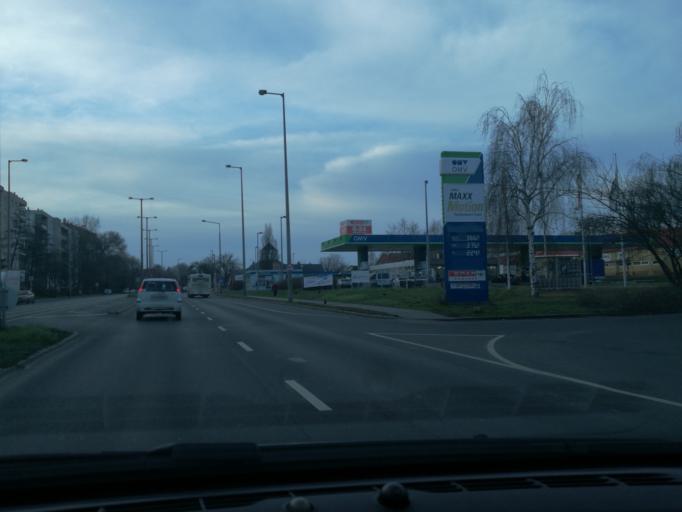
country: HU
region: Szabolcs-Szatmar-Bereg
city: Nyiregyhaza
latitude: 47.9466
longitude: 21.7260
